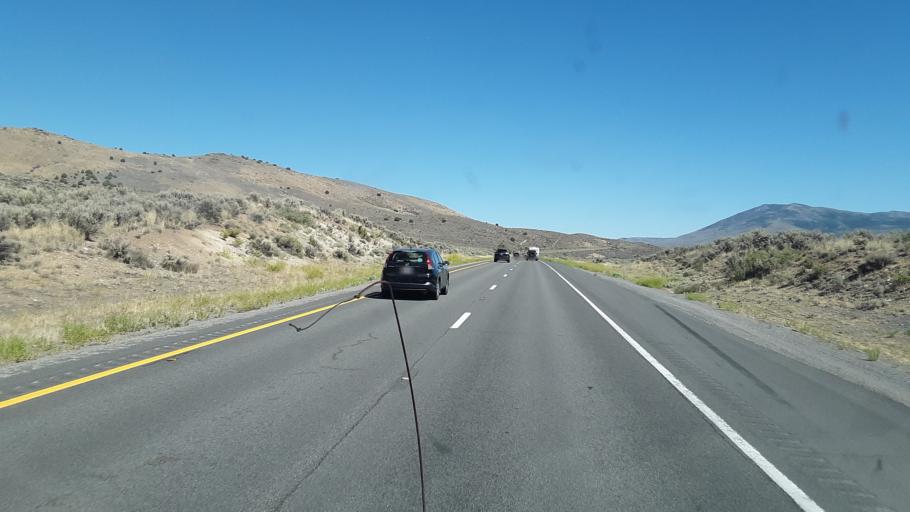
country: US
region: Nevada
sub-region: Washoe County
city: Cold Springs
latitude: 39.6944
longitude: -120.0229
